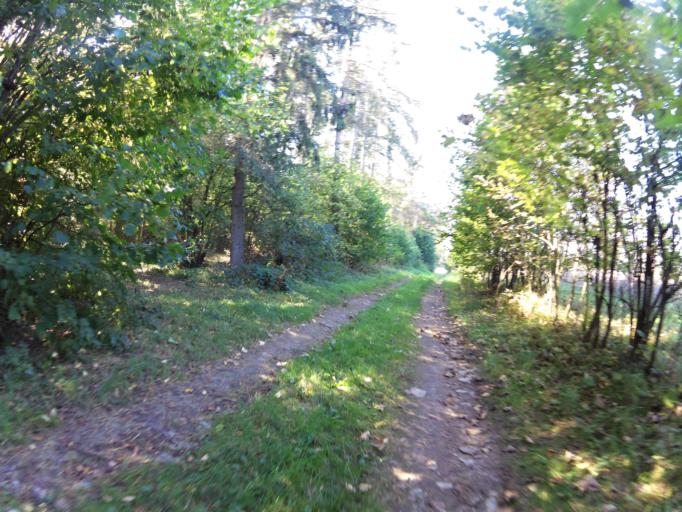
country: DE
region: Bavaria
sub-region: Regierungsbezirk Unterfranken
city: Ochsenfurt
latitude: 49.6864
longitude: 10.0472
